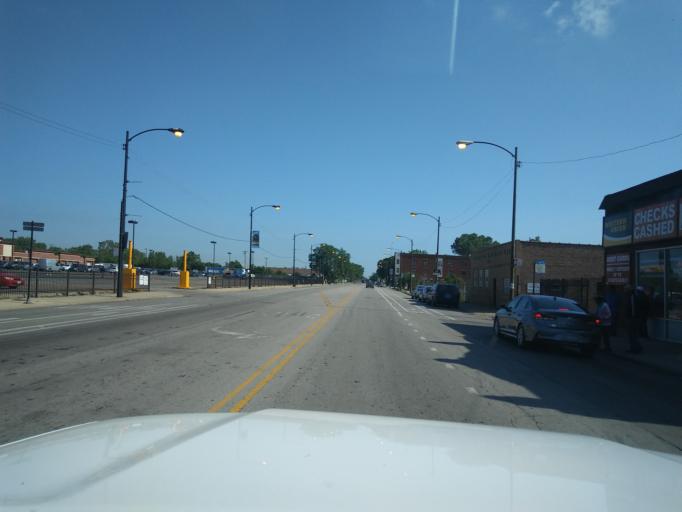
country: US
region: Illinois
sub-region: Cook County
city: Chicago
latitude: 41.8090
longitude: -87.6455
